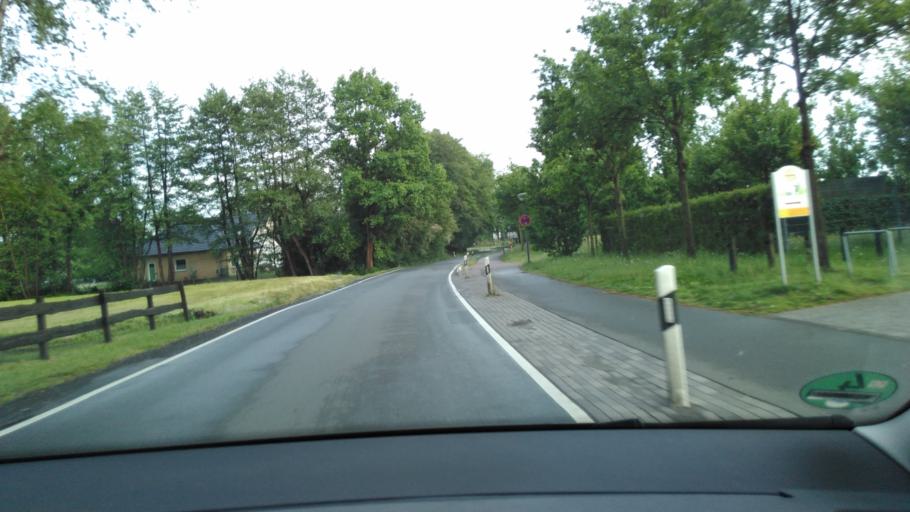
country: DE
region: North Rhine-Westphalia
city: Rietberg
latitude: 51.8215
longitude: 8.4461
